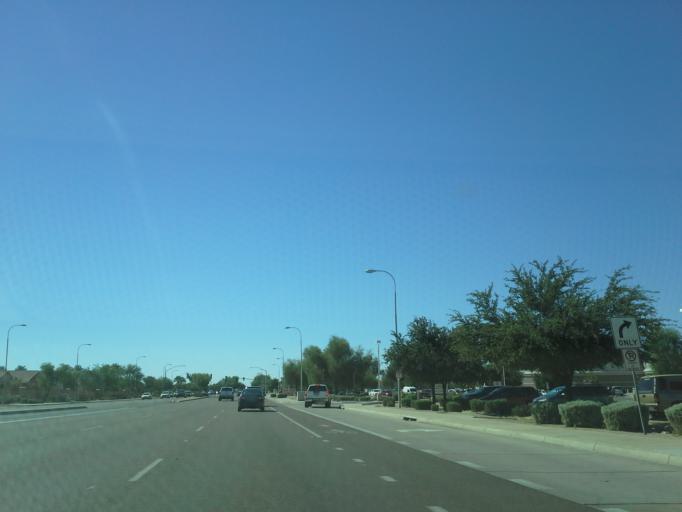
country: US
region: Arizona
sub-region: Maricopa County
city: Chandler
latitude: 33.2538
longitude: -111.8414
